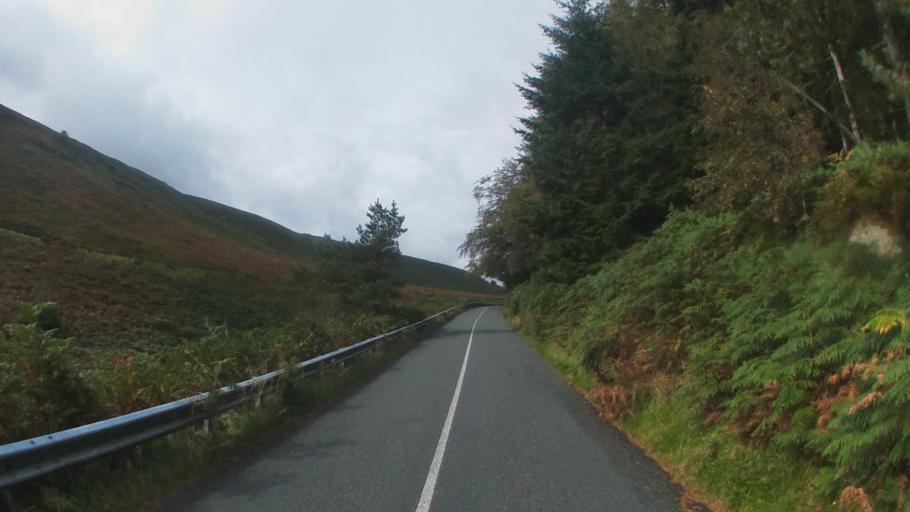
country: IE
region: Leinster
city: Ballinteer
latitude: 53.2318
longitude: -6.2742
